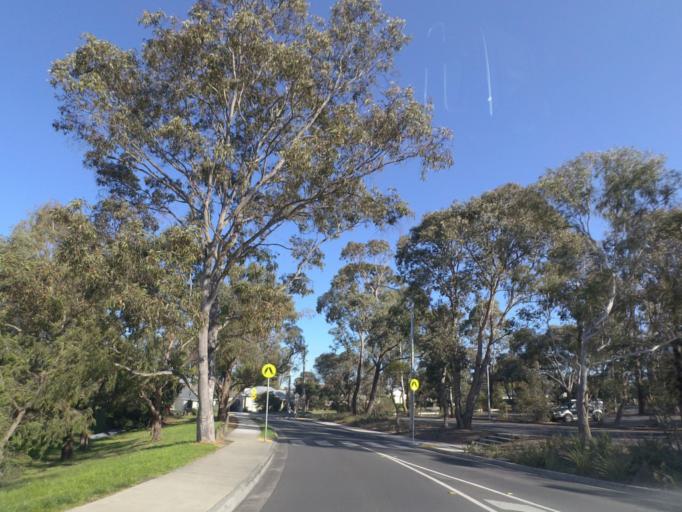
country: AU
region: Victoria
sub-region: Maroondah
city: Heathmont
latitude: -37.8258
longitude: 145.2305
